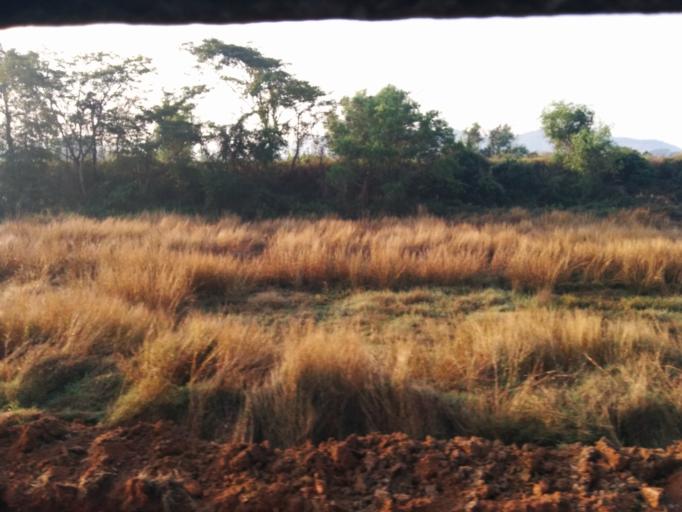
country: IN
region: Goa
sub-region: South Goa
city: Davorlim
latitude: 15.2666
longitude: 73.9962
